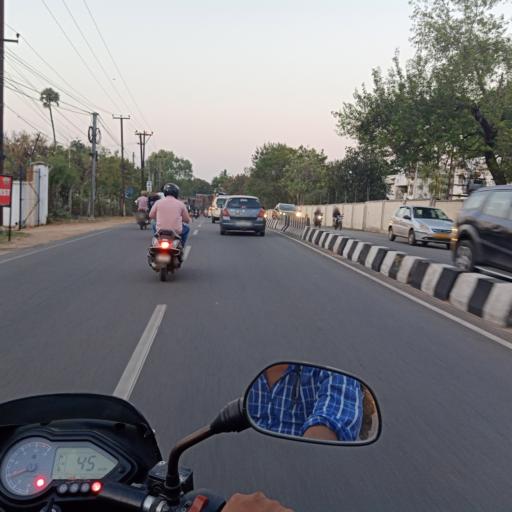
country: IN
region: Telangana
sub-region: Rangareddi
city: Secunderabad
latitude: 17.4897
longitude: 78.5125
